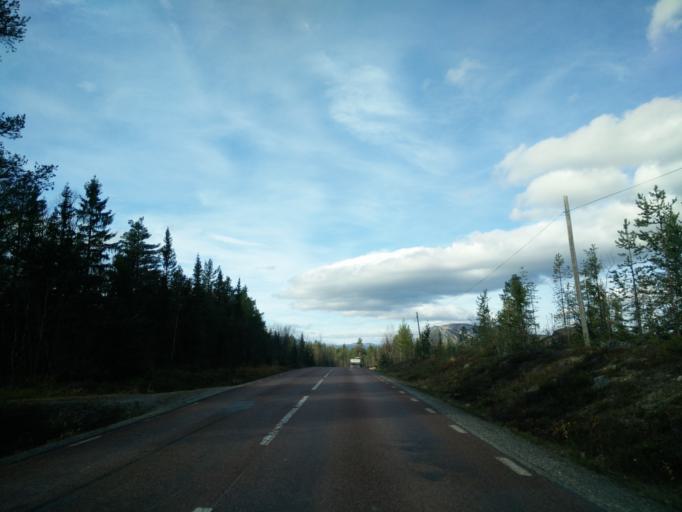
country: NO
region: Hedmark
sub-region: Engerdal
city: Engerdal
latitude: 62.5072
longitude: 12.6139
